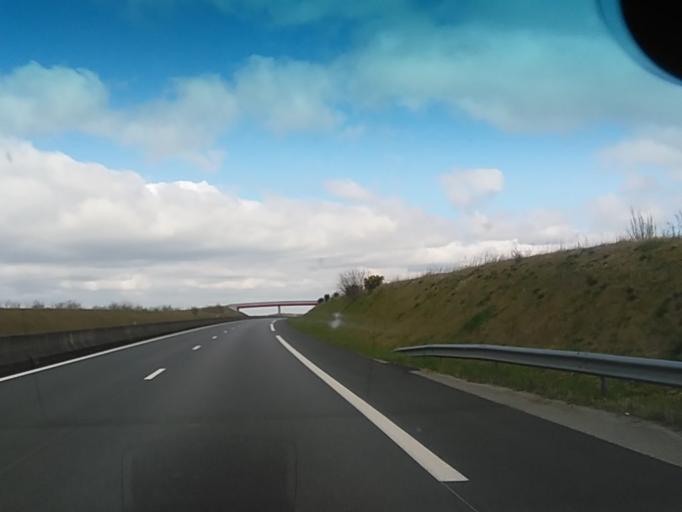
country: FR
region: Lower Normandy
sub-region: Departement du Calvados
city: Orbec
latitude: 48.9945
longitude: 0.4410
